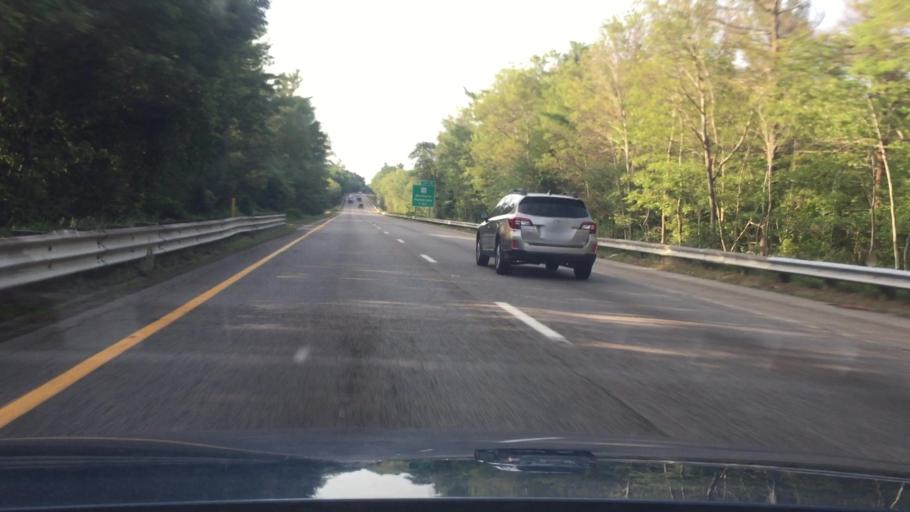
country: US
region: Massachusetts
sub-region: Plymouth County
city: Marshfield
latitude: 42.0725
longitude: -70.7334
